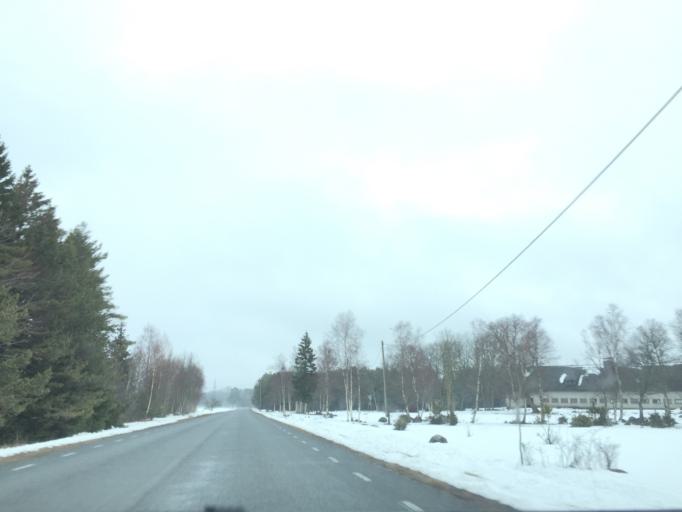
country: EE
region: Saare
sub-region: Kuressaare linn
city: Kuressaare
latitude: 58.3474
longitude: 22.0318
